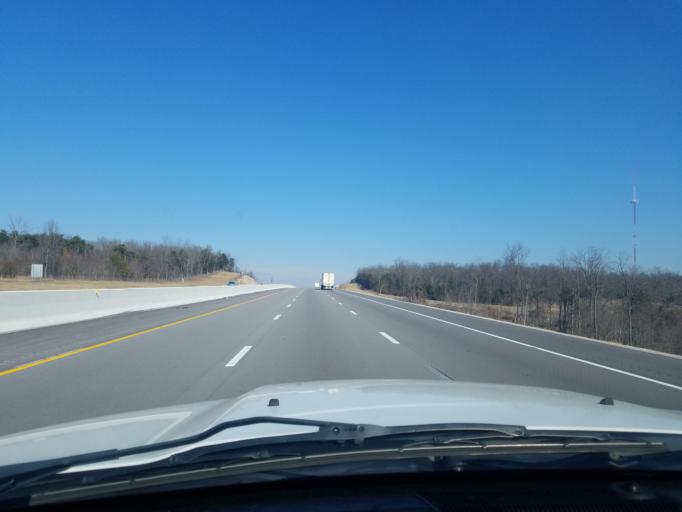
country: US
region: Kentucky
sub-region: Hart County
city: Munfordville
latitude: 37.4441
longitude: -85.8836
